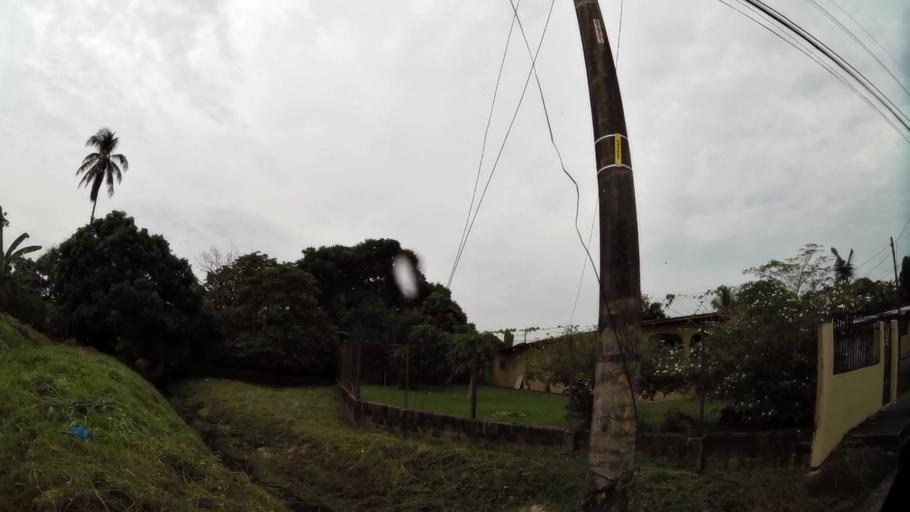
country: PA
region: Panama
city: San Miguelito
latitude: 9.0415
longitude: -79.4397
